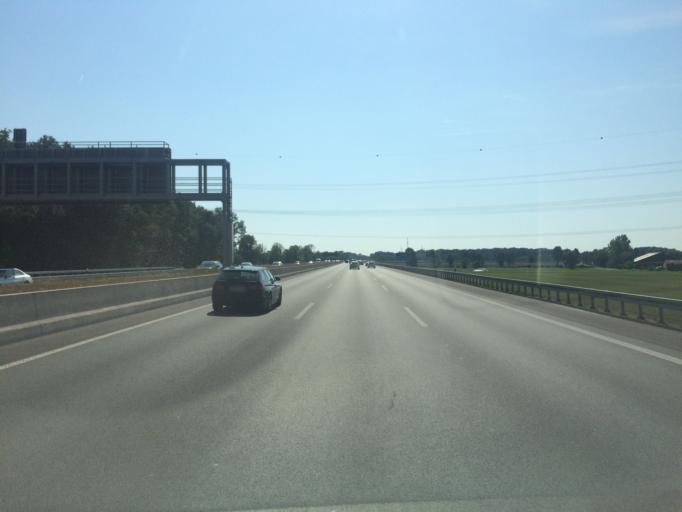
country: DE
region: North Rhine-Westphalia
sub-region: Regierungsbezirk Munster
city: Muenster
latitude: 51.9047
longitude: 7.5661
